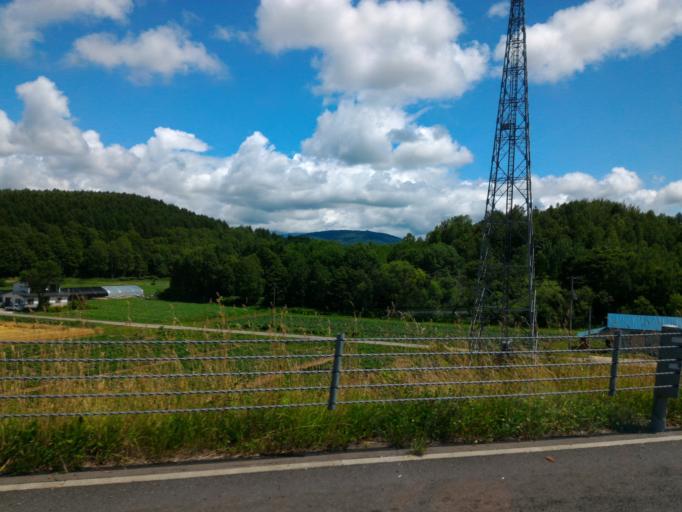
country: JP
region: Hokkaido
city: Nayoro
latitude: 44.4116
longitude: 142.4049
